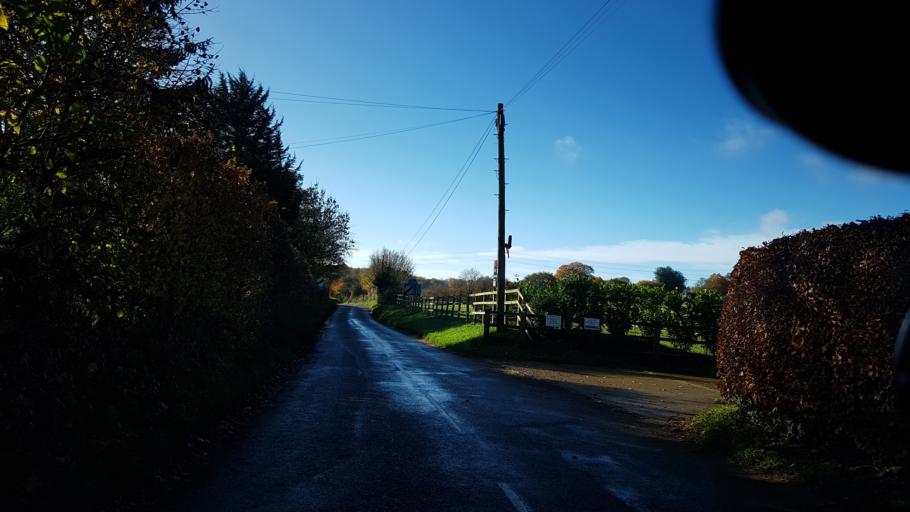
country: GB
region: England
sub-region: Surrey
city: Normandy
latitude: 51.2183
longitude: -0.6716
